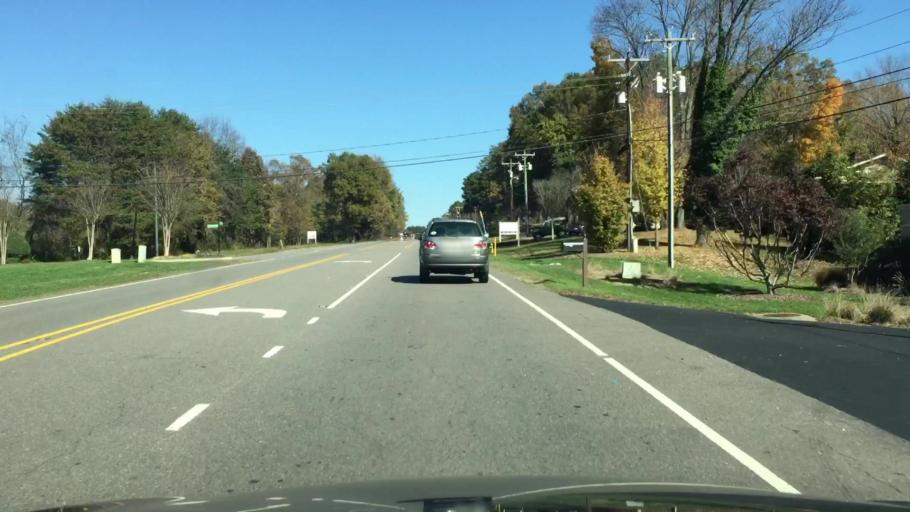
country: US
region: North Carolina
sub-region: Iredell County
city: Mooresville
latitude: 35.5700
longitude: -80.8452
